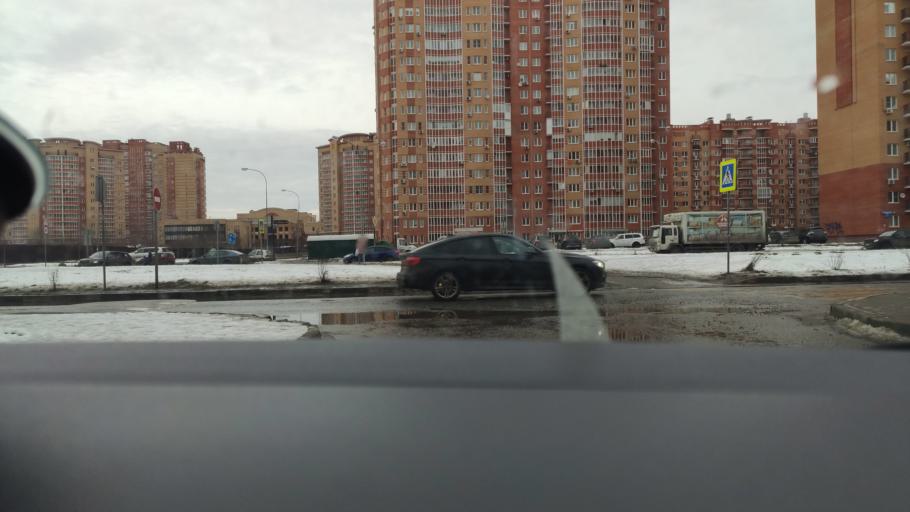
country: RU
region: Moskovskaya
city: Lesnoy Gorodok
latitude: 55.6574
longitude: 37.2286
